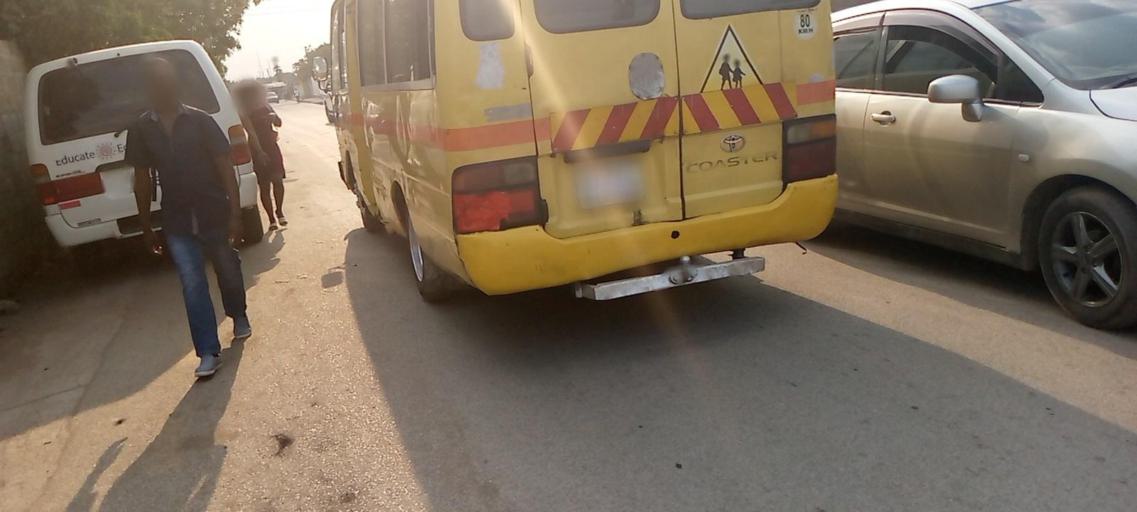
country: ZM
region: Lusaka
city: Lusaka
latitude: -15.4040
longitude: 28.3466
